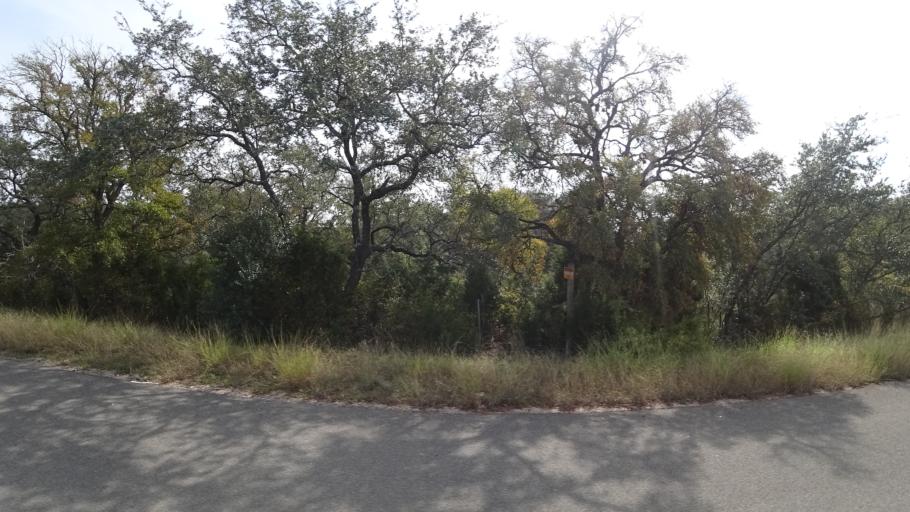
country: US
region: Texas
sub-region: Travis County
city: Hudson Bend
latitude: 30.3901
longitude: -97.9400
